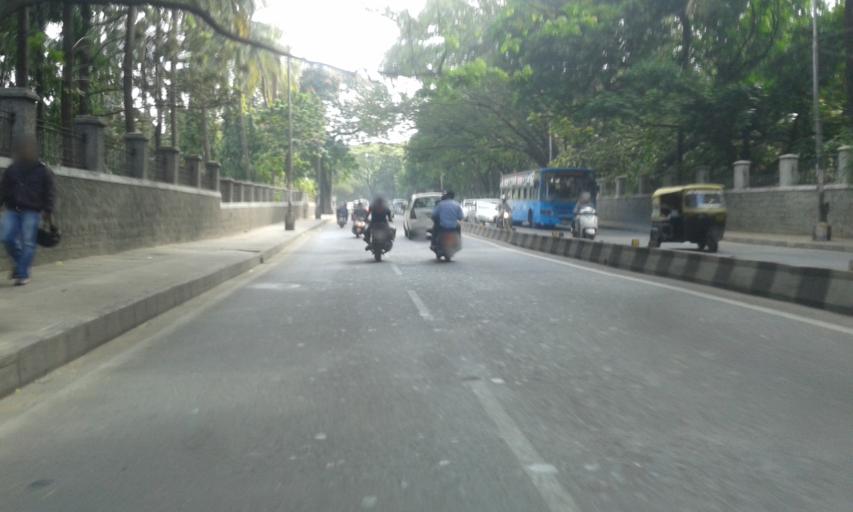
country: IN
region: Karnataka
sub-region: Bangalore Urban
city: Bangalore
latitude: 12.9417
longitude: 77.5975
